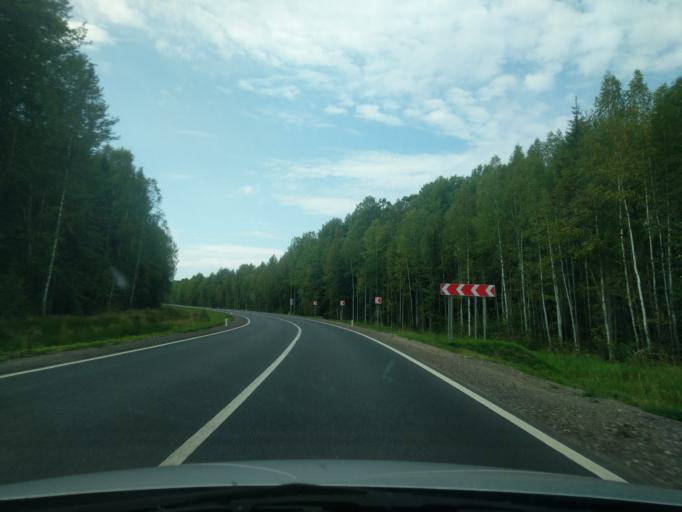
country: RU
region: Kostroma
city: Kadyy
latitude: 57.8528
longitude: 43.4933
